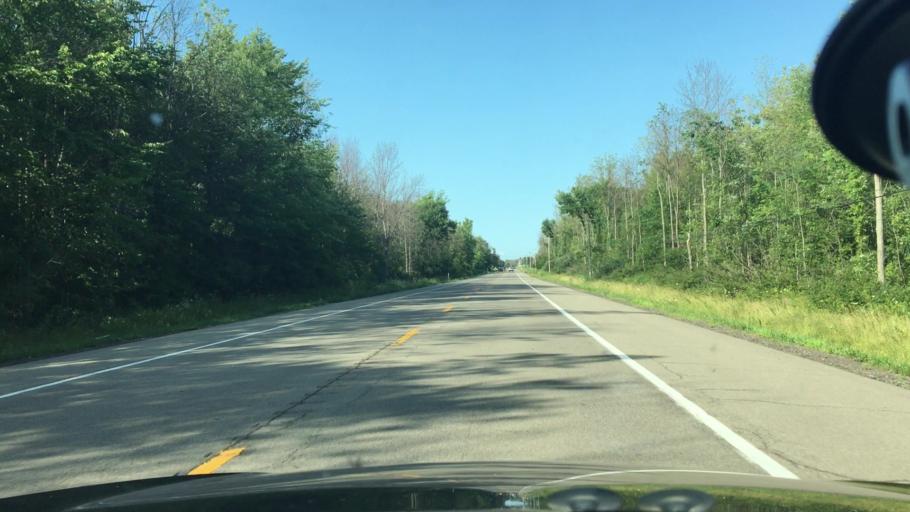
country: US
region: New York
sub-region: Erie County
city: Eden
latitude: 42.6702
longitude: -78.9605
